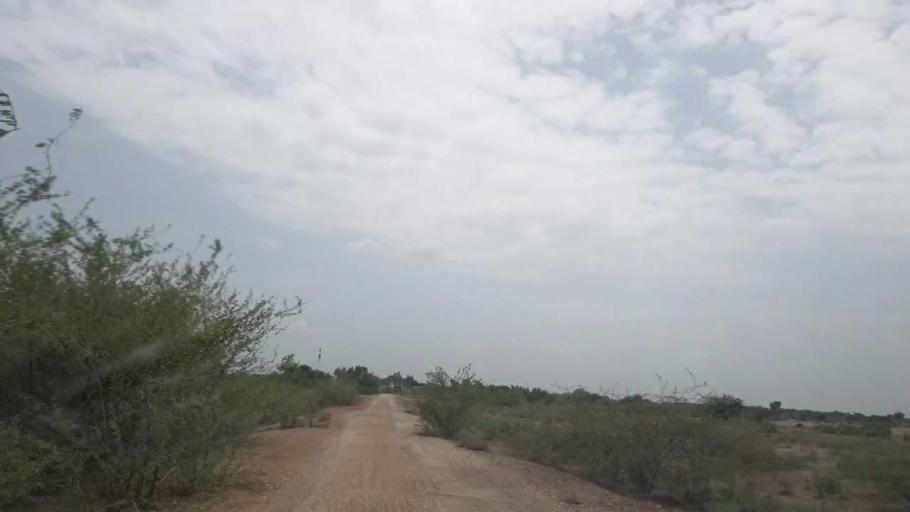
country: PK
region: Sindh
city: Naukot
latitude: 24.9093
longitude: 69.2022
